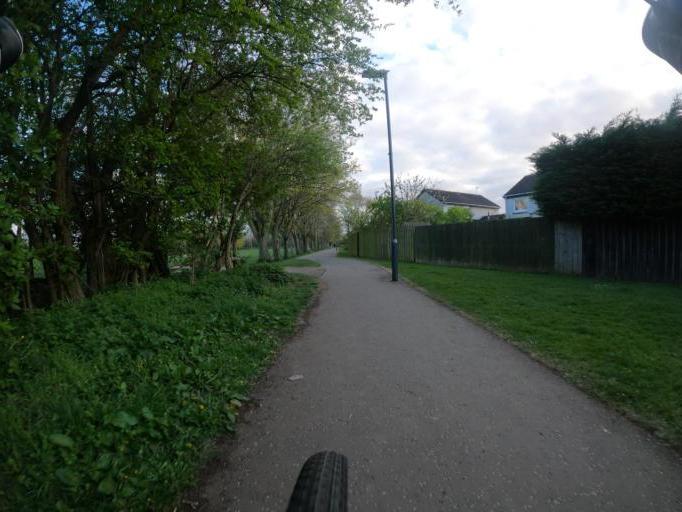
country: GB
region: Scotland
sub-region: Edinburgh
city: Currie
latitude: 55.9404
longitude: -3.3066
